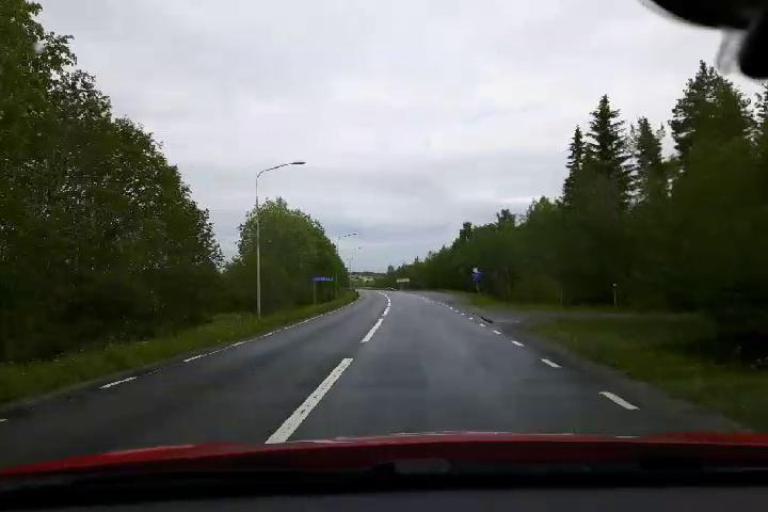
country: SE
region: Jaemtland
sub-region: Bergs Kommun
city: Hoverberg
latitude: 62.9802
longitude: 14.4535
